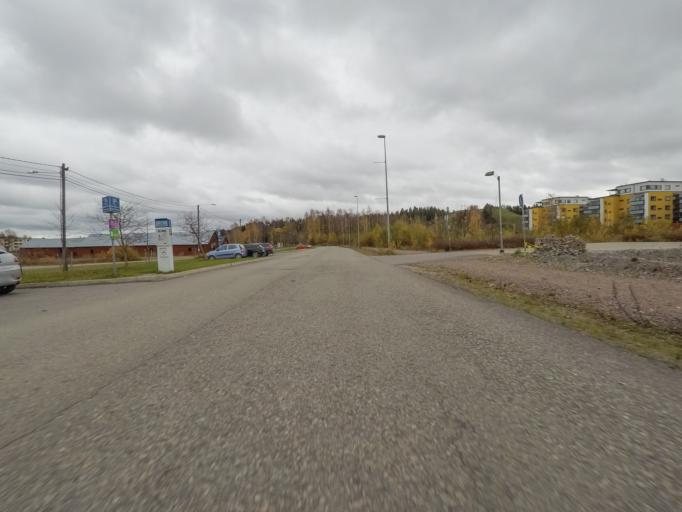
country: FI
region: Uusimaa
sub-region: Porvoo
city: Porvoo
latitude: 60.3884
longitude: 25.6593
